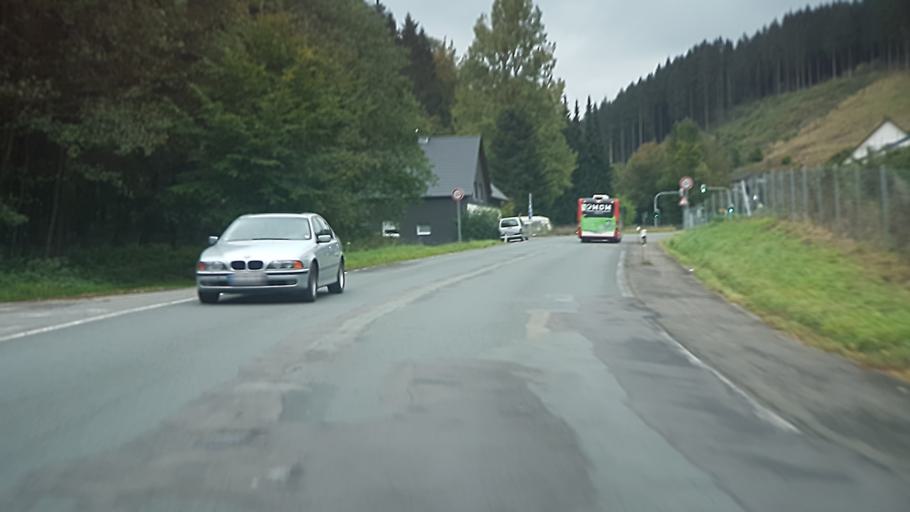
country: DE
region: North Rhine-Westphalia
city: Plettenberg
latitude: 51.1578
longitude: 7.8477
